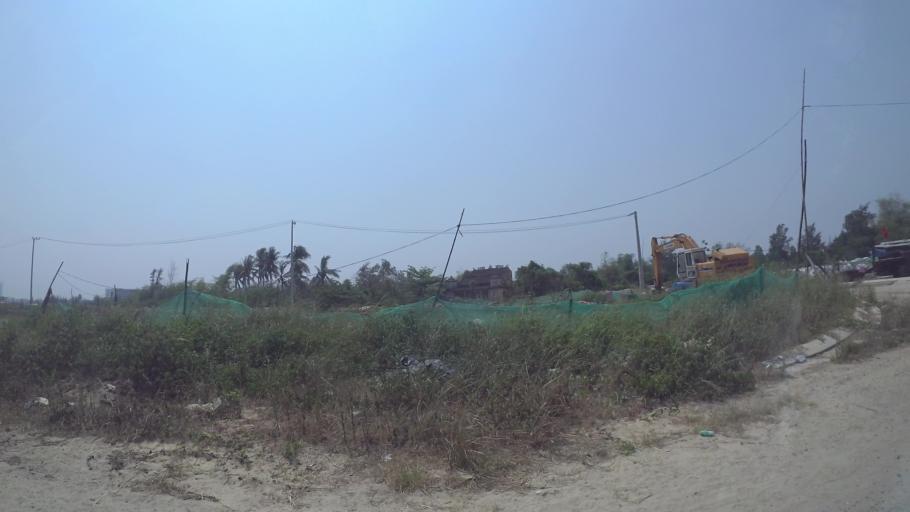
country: VN
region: Da Nang
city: Ngu Hanh Son
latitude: 15.9851
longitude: 108.2591
